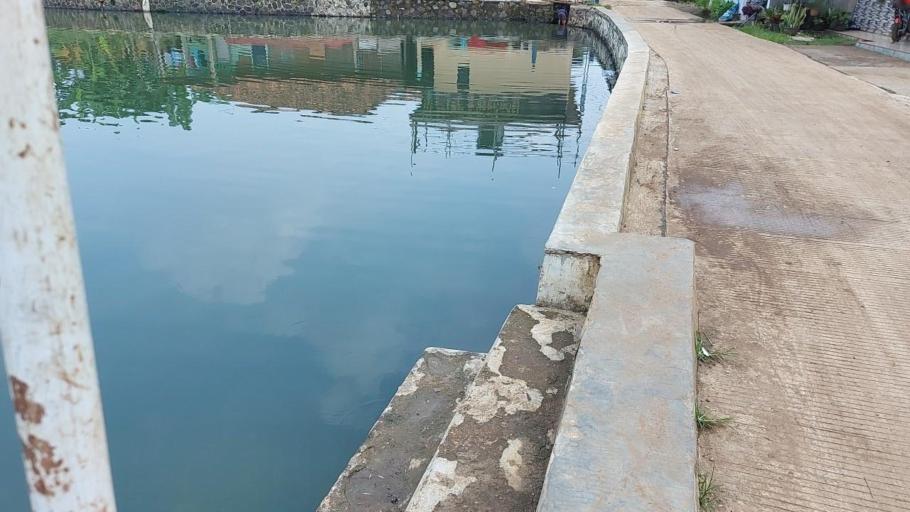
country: ID
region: West Java
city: Cibinong
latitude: -6.5286
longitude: 106.8166
